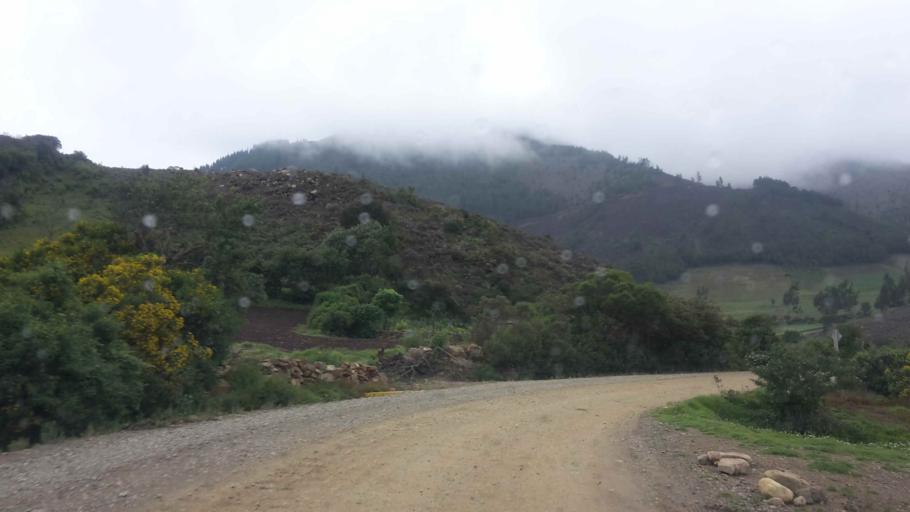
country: BO
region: Cochabamba
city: Totora
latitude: -17.5837
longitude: -65.2928
